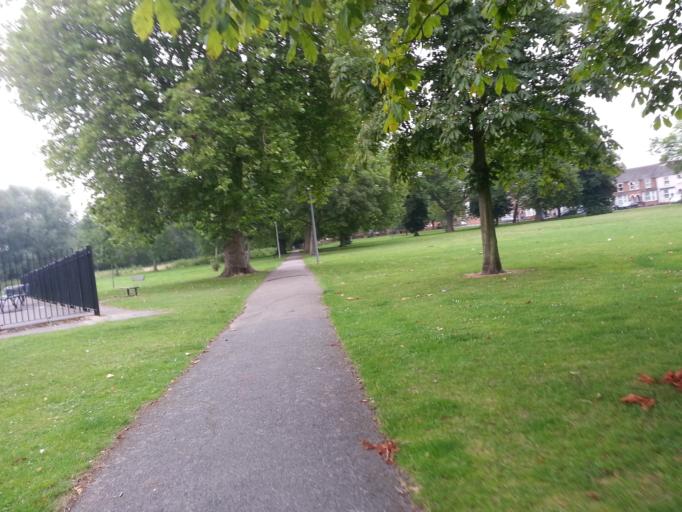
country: GB
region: England
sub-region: Suffolk
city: Ipswich
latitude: 52.0556
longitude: 1.1431
